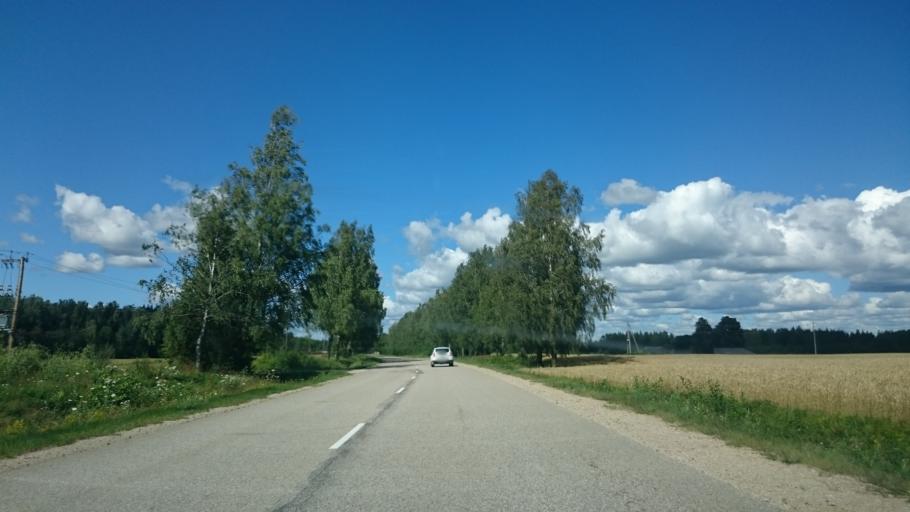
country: LV
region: Kuldigas Rajons
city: Kuldiga
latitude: 56.8938
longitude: 21.8872
